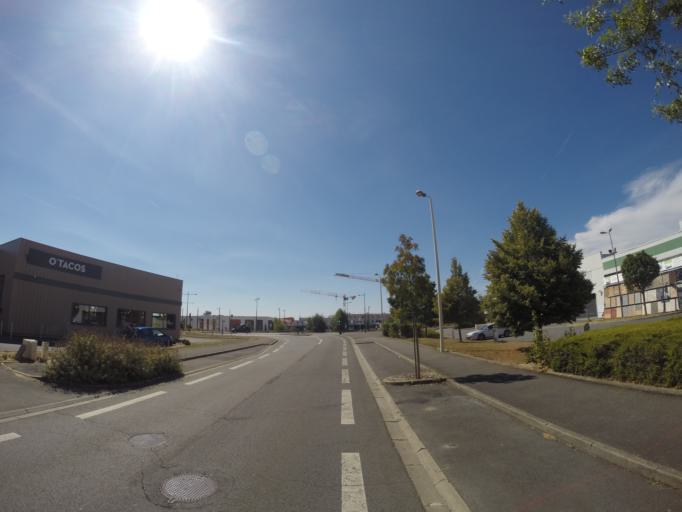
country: FR
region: Centre
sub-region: Departement d'Indre-et-Loire
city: Parcay-Meslay
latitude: 47.4245
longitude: 0.7097
